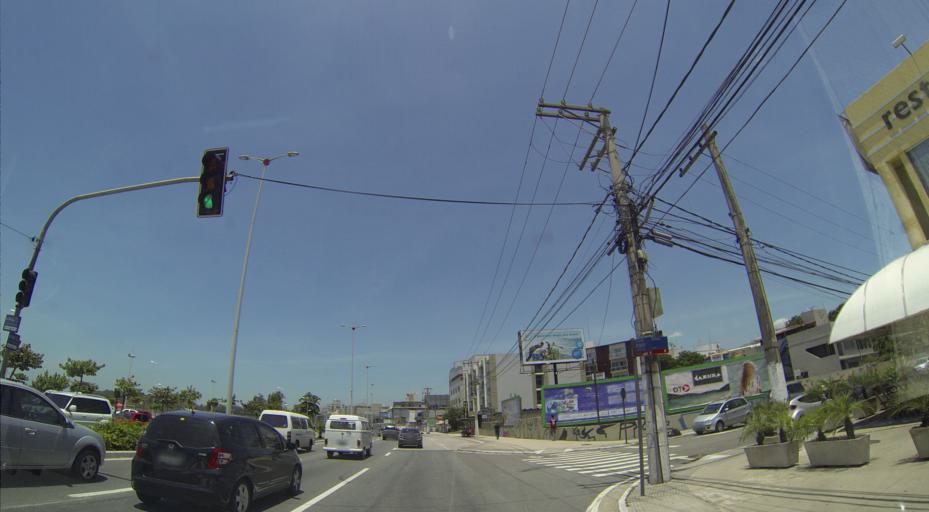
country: BR
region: Espirito Santo
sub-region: Vila Velha
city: Vila Velha
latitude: -20.2849
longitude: -40.2907
